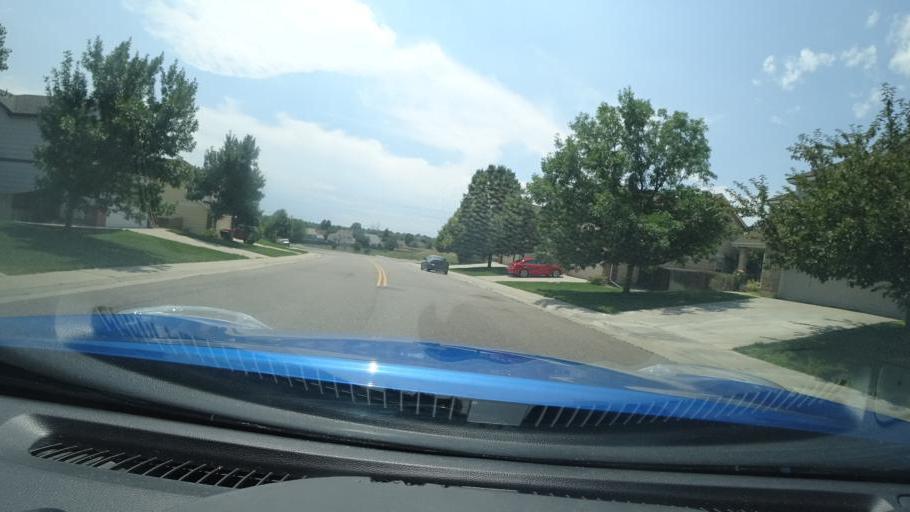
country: US
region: Colorado
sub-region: Adams County
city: Aurora
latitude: 39.6691
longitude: -104.7586
